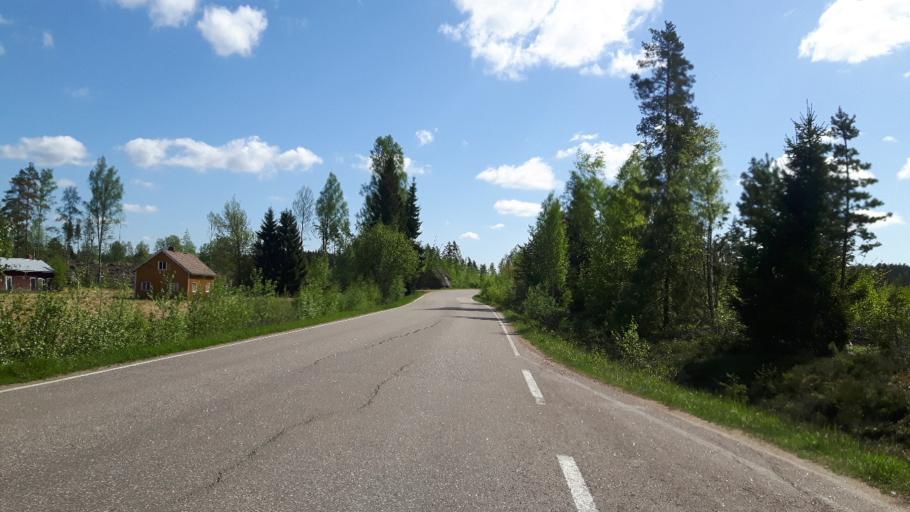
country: FI
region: Kymenlaakso
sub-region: Kotka-Hamina
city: Hamina
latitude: 60.5257
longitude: 27.3044
